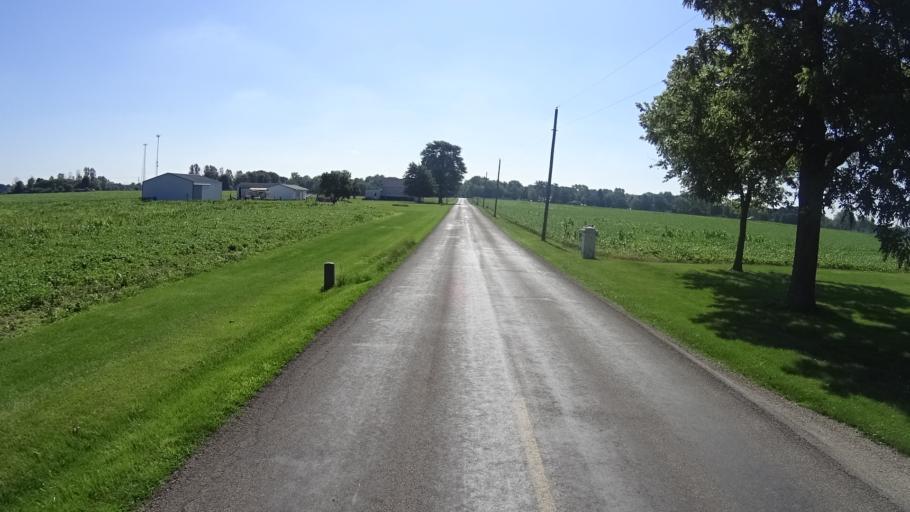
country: US
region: Indiana
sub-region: Madison County
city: Ingalls
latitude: 39.9879
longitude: -85.8010
